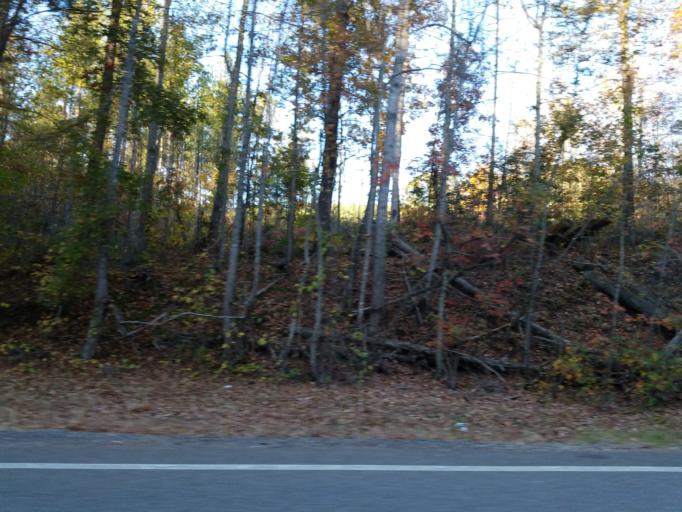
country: US
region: Georgia
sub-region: Dawson County
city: Dawsonville
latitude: 34.5439
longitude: -84.2222
